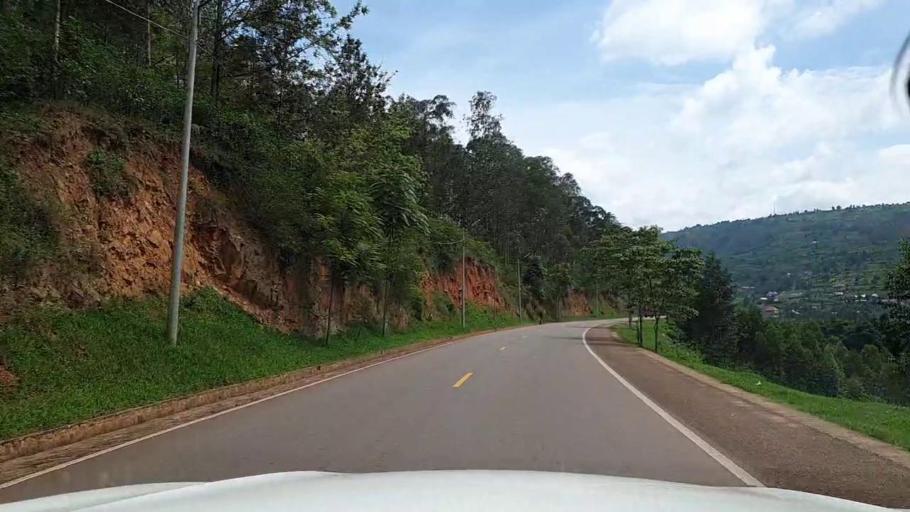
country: RW
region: Kigali
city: Kigali
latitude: -1.8601
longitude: 30.0911
